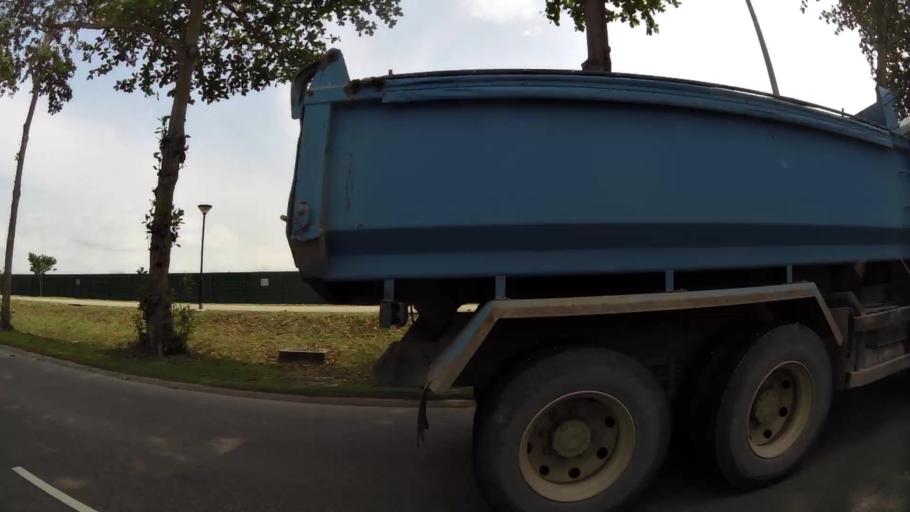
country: SG
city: Singapore
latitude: 1.3557
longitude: 103.9993
